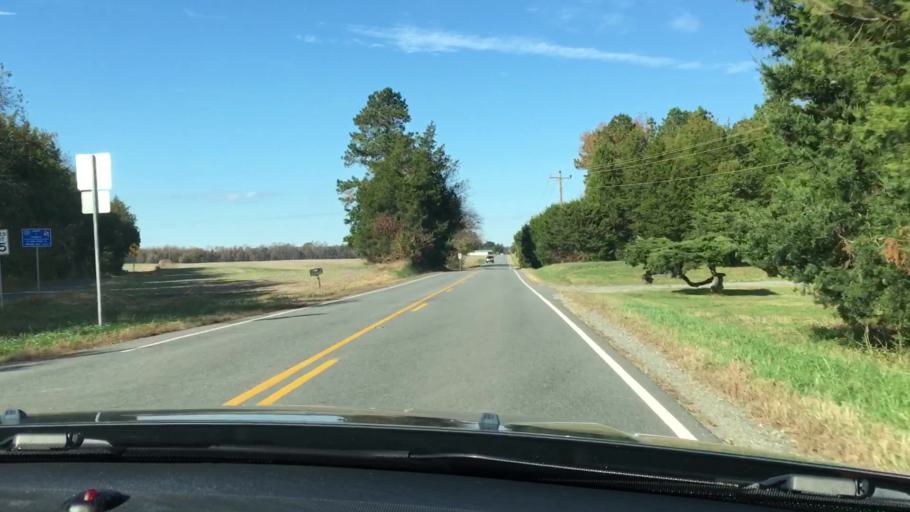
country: US
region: Virginia
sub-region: King and Queen County
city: King and Queen Court House
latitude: 37.6255
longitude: -76.9307
